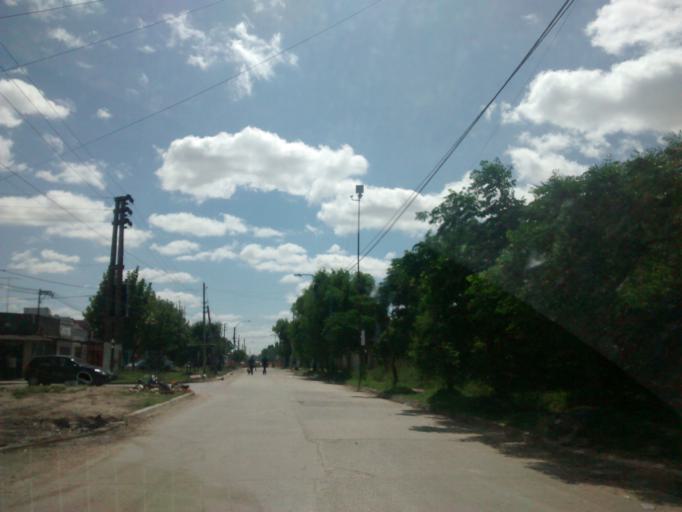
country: AR
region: Buenos Aires
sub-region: Partido de Berisso
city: Berisso
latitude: -34.8835
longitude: -57.8656
